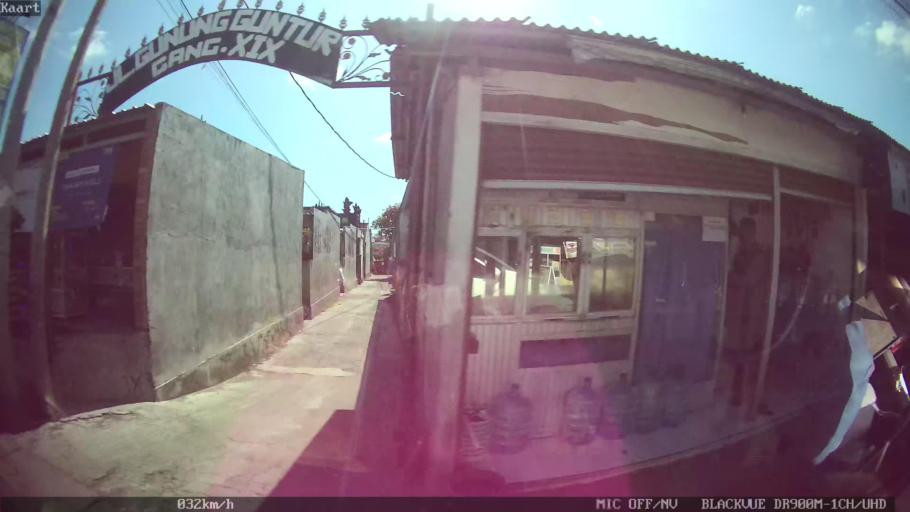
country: ID
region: Bali
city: Denpasar
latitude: -8.6525
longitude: 115.1808
